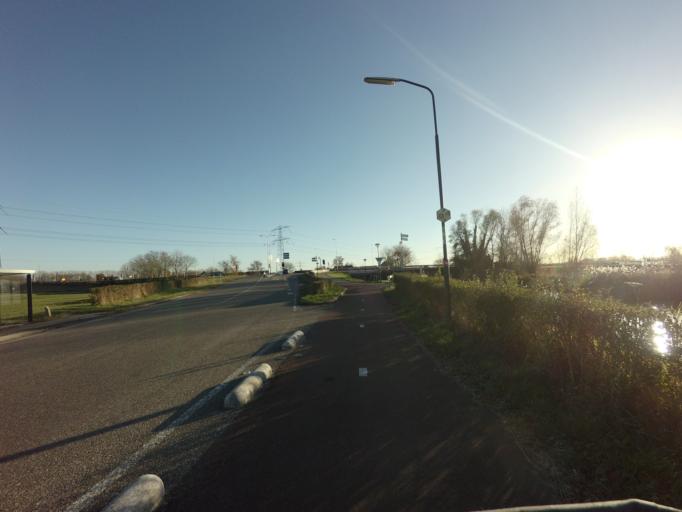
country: NL
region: Utrecht
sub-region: Stichtse Vecht
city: Vreeland
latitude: 52.2274
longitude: 4.9982
